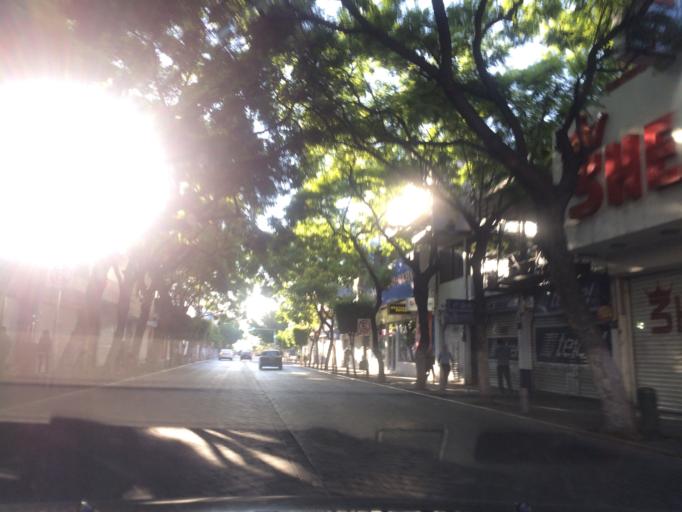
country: MX
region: Puebla
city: Tehuacan
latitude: 18.4630
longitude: -97.3940
